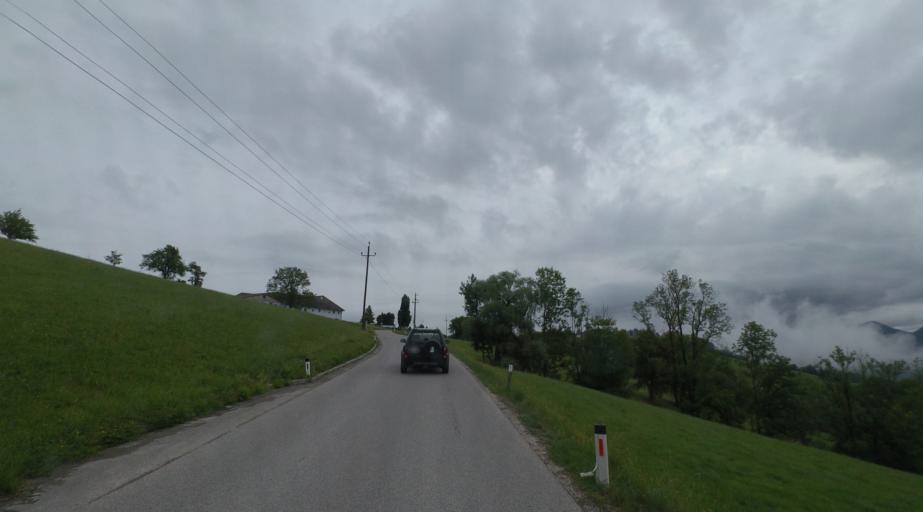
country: AT
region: Upper Austria
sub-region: Politischer Bezirk Kirchdorf an der Krems
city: Micheldorf in Oberoesterreich
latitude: 47.9236
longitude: 14.1627
